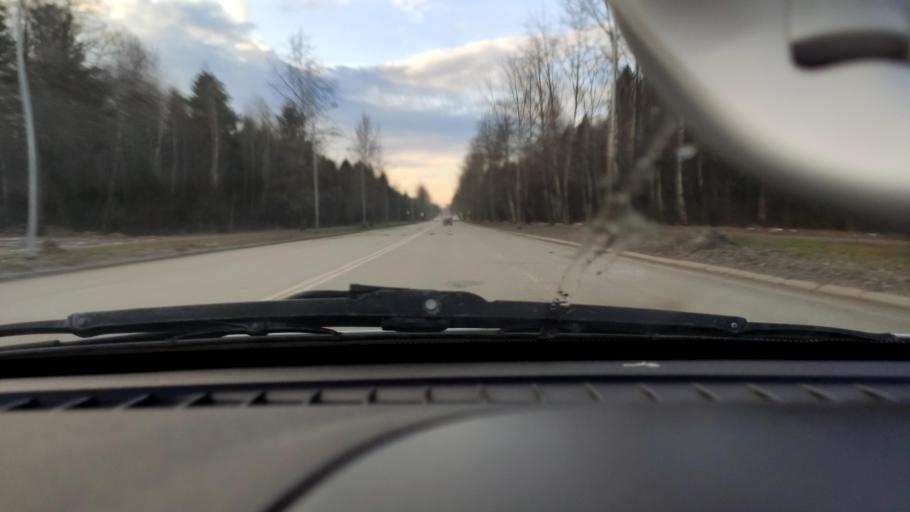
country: RU
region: Perm
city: Perm
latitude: 58.0887
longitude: 56.3807
